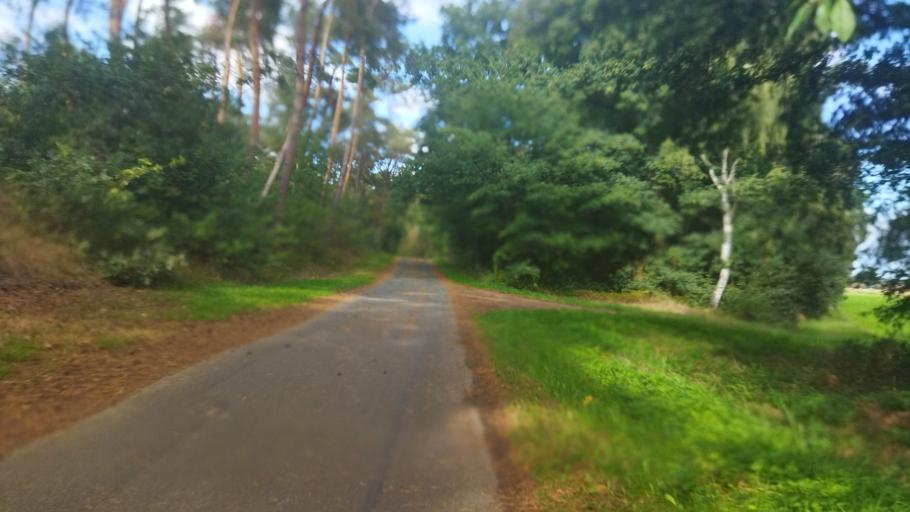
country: DE
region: North Rhine-Westphalia
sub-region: Regierungsbezirk Munster
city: Dulmen
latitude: 51.7956
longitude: 7.2577
